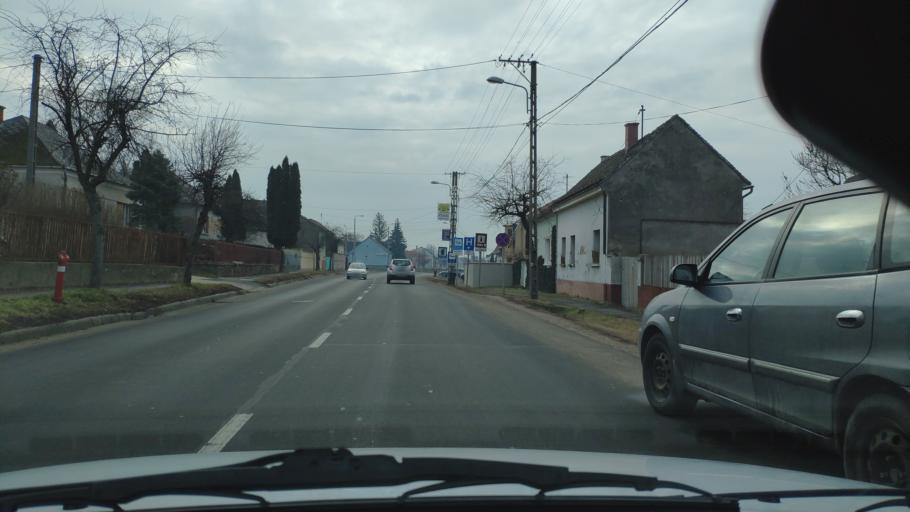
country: HU
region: Zala
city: Nagykanizsa
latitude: 46.4680
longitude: 16.9857
